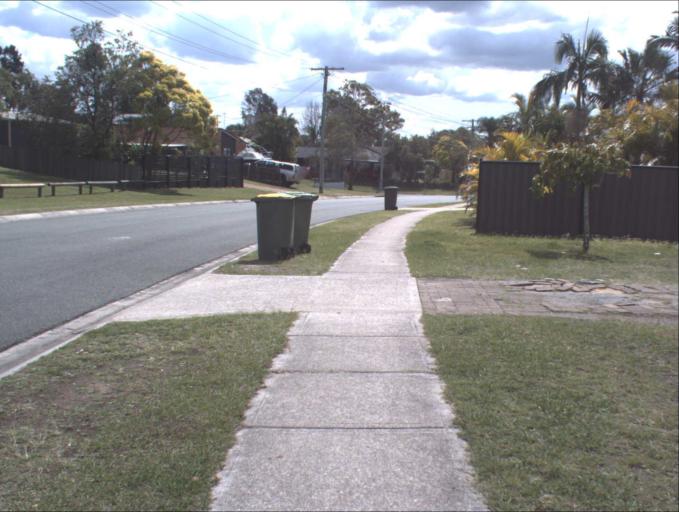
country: AU
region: Queensland
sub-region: Logan
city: Waterford West
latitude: -27.6857
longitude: 153.1510
